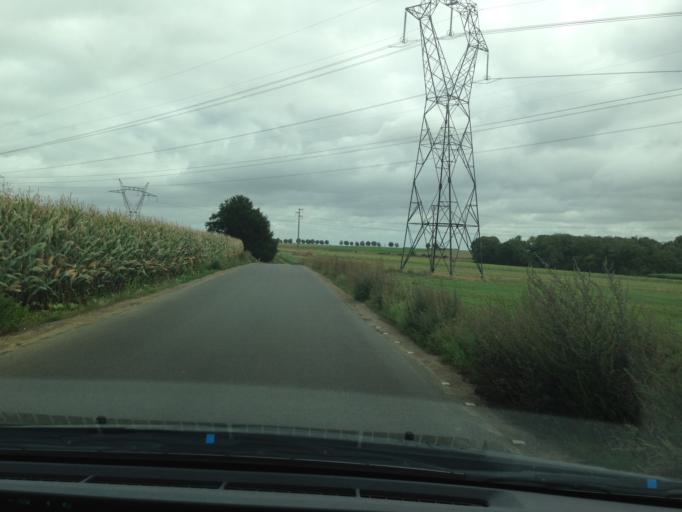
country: FR
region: Ile-de-France
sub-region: Departement du Val-d'Oise
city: Ennery
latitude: 49.0873
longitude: 2.0997
